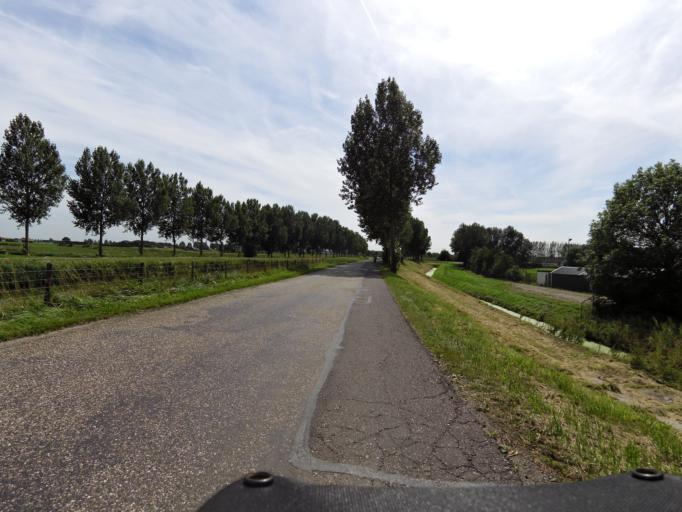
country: NL
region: South Holland
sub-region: Gemeente Goeree-Overflakkee
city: Dirksland
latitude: 51.7576
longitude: 4.1053
